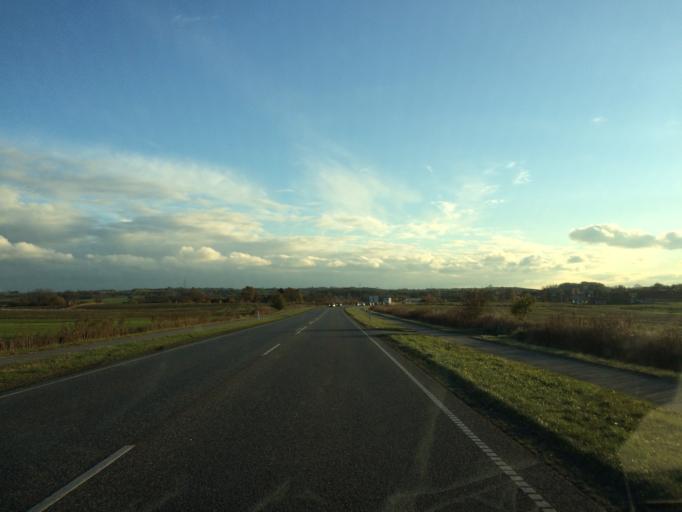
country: DK
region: South Denmark
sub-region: Sonderborg Kommune
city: Augustenborg
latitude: 54.9584
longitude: 9.8996
